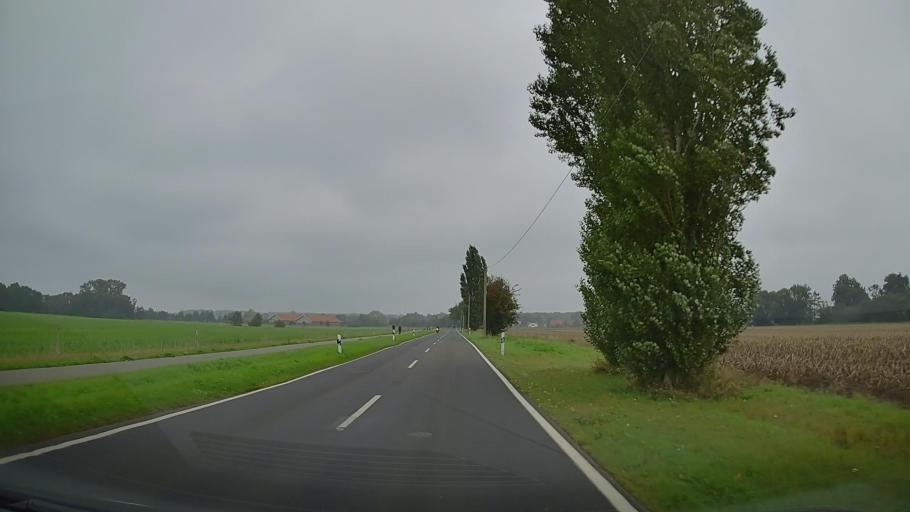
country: DE
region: Mecklenburg-Vorpommern
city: Neubukow
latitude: 54.0679
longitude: 11.6292
